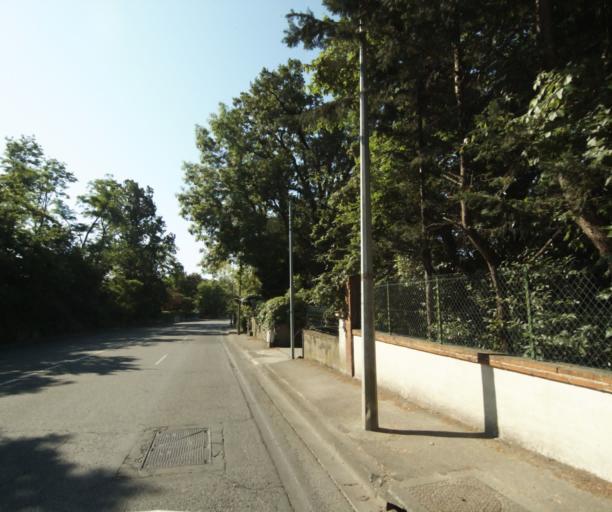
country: FR
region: Midi-Pyrenees
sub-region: Departement du Tarn-et-Garonne
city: Montauban
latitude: 44.0071
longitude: 1.3606
